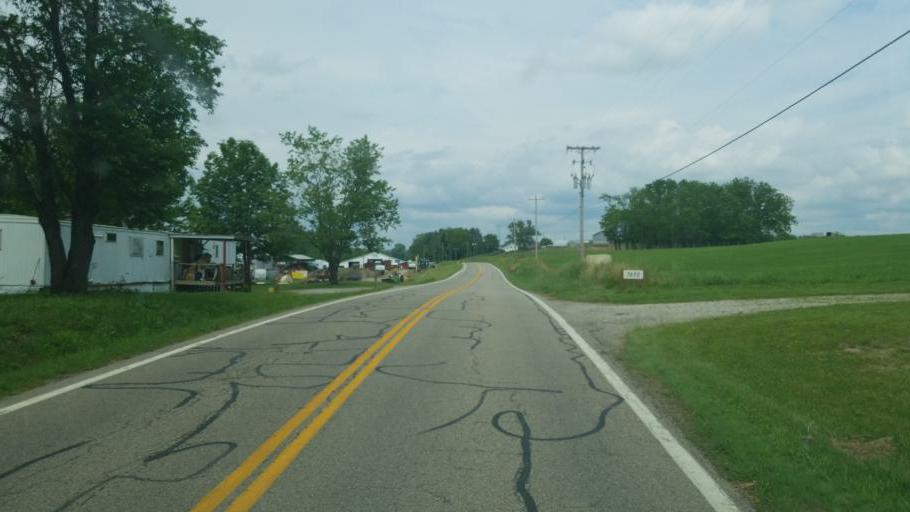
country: US
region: Ohio
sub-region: Perry County
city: Thornport
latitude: 39.9040
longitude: -82.3800
